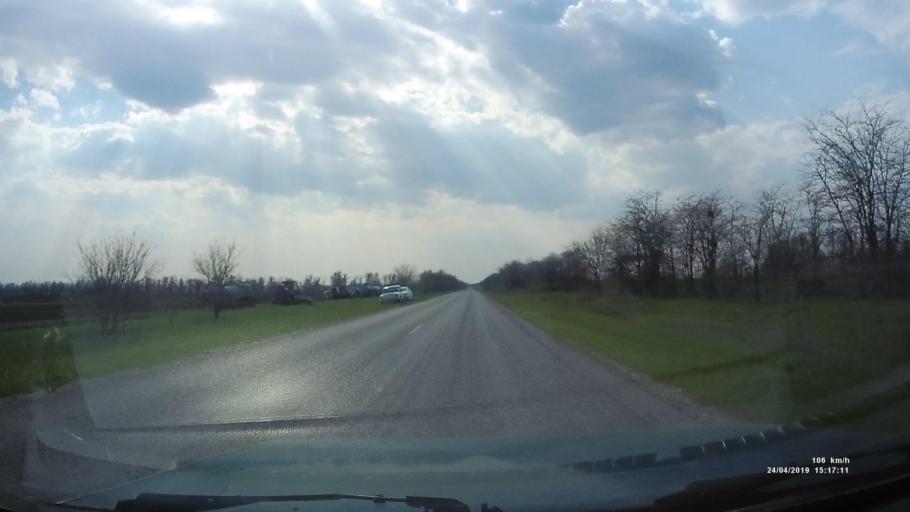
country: RU
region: Rostov
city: Remontnoye
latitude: 46.5465
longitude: 43.1956
